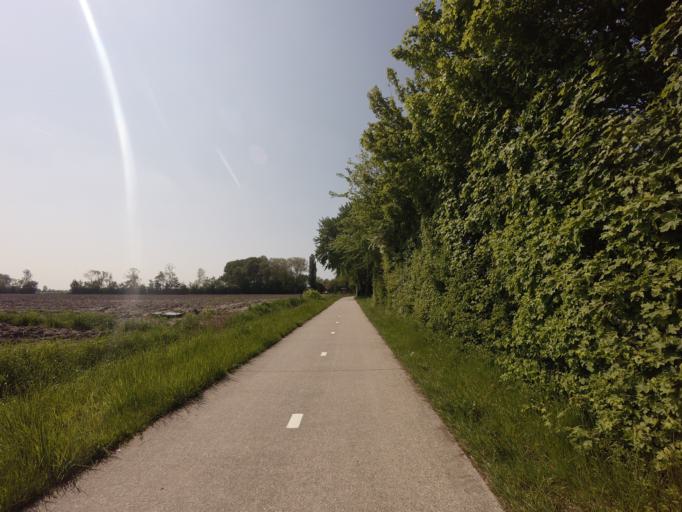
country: NL
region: Zeeland
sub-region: Gemeente Veere
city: Veere
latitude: 51.5462
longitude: 3.6456
